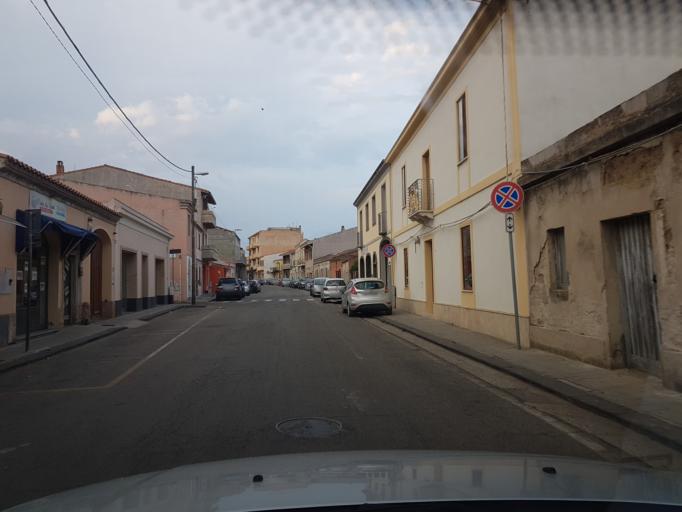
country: IT
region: Sardinia
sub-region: Provincia di Oristano
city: Cabras
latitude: 39.9289
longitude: 8.5326
